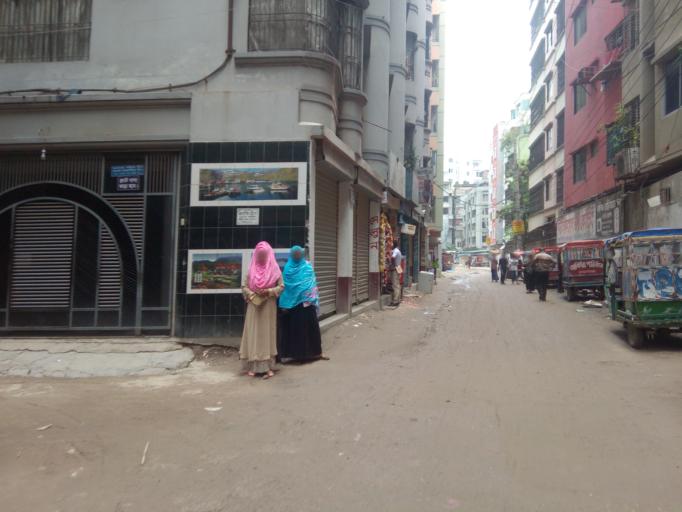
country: BD
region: Dhaka
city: Paltan
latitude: 23.7613
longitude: 90.4322
